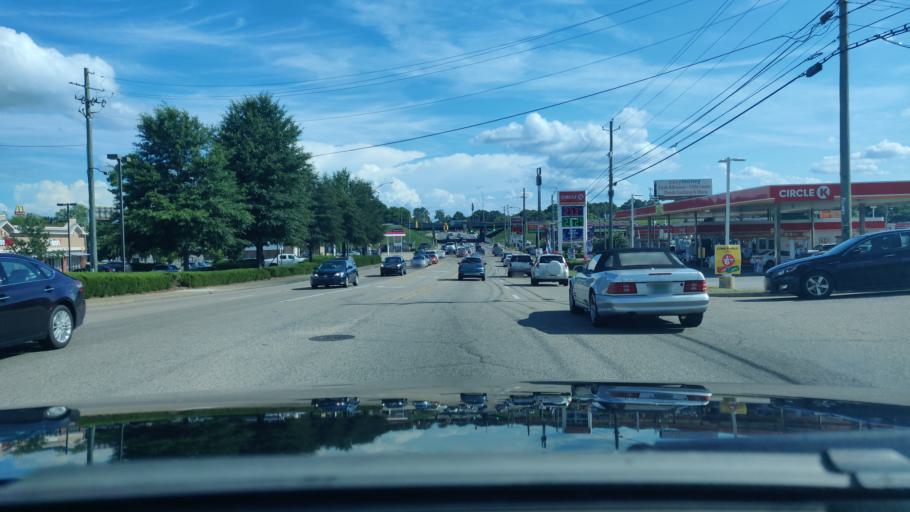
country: US
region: Alabama
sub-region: Montgomery County
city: Montgomery
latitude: 32.3693
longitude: -86.2710
